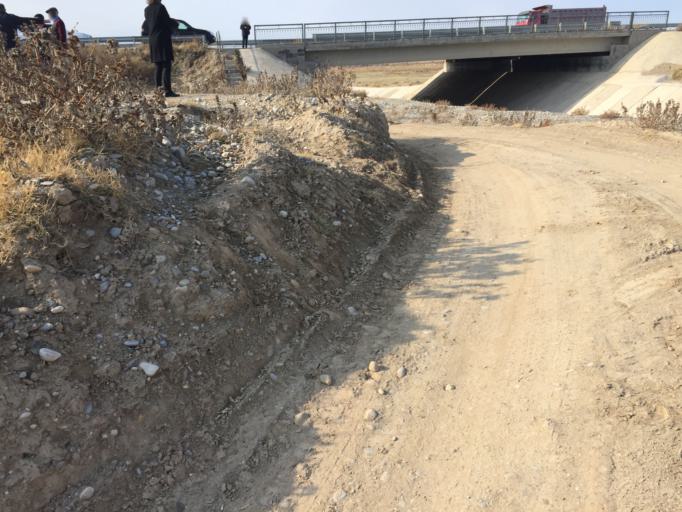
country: KZ
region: Ongtustik Qazaqstan
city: Temirlanovka
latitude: 42.5900
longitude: 69.3096
